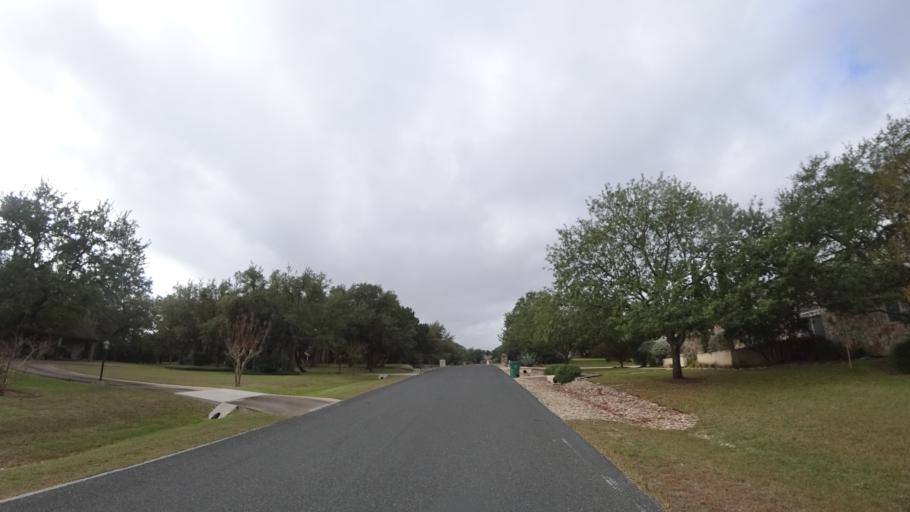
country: US
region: Texas
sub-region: Travis County
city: Barton Creek
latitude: 30.2545
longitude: -97.9077
